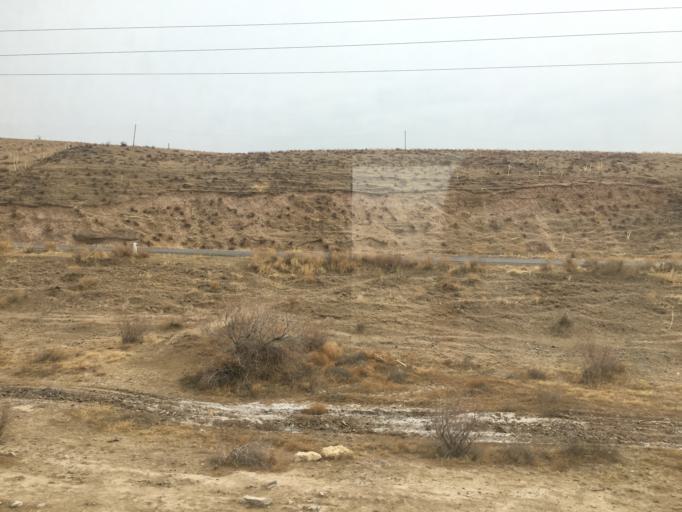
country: TM
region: Mary
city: Serhetabat
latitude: 35.5013
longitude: 62.4700
